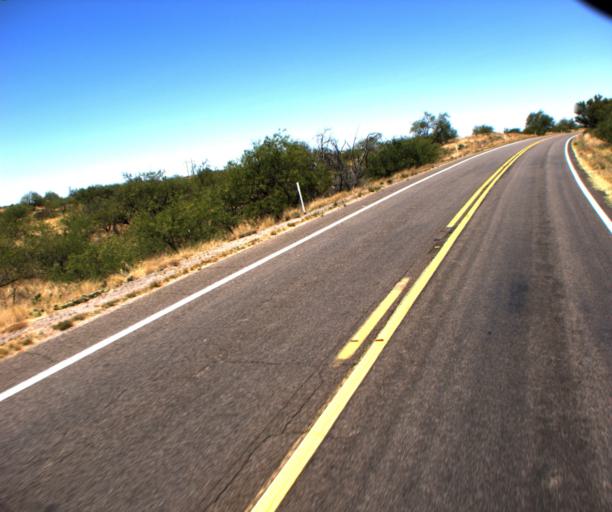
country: US
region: Arizona
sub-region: Pima County
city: Catalina
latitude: 32.6057
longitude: -110.9851
